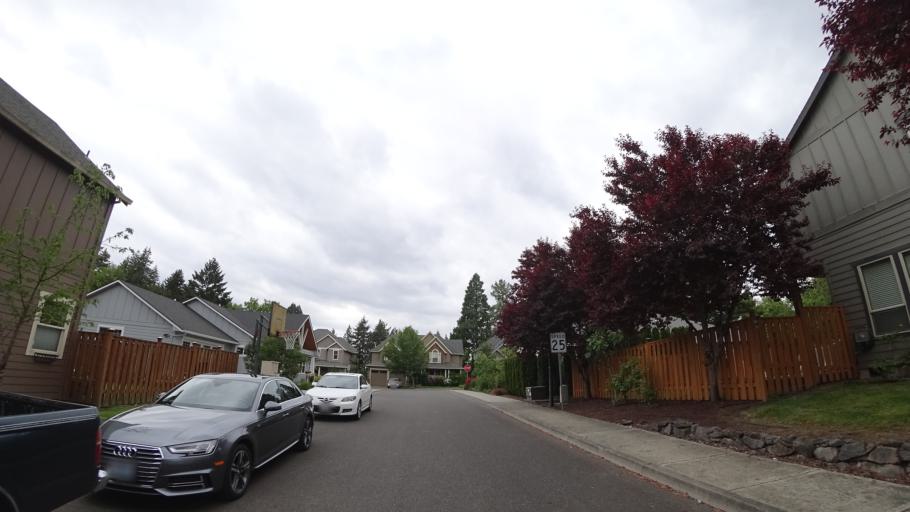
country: US
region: Oregon
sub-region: Washington County
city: West Slope
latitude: 45.4900
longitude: -122.7787
